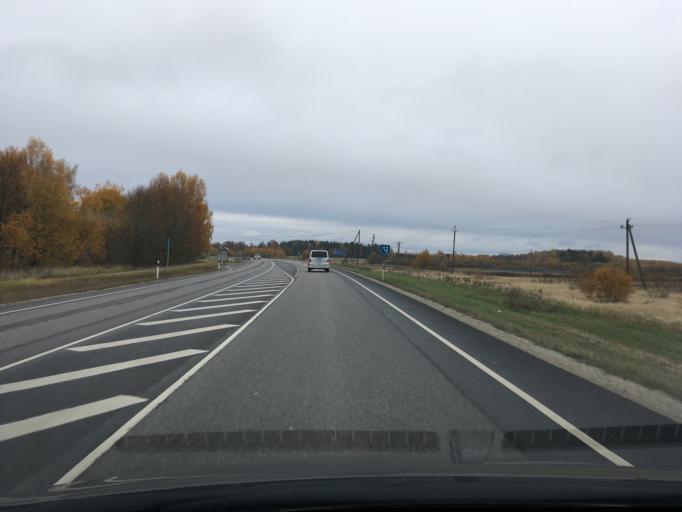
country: EE
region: Tartu
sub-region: UElenurme vald
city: Ulenurme
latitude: 58.3263
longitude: 26.6408
